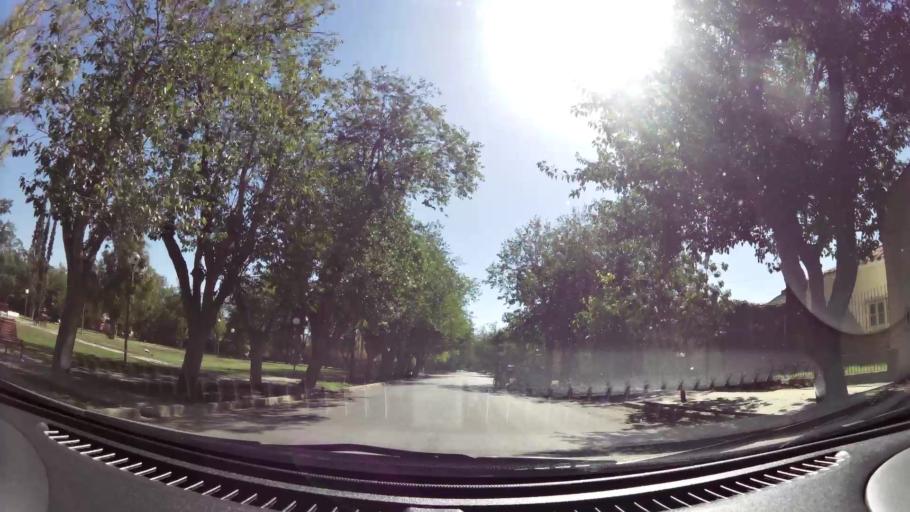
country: AR
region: Mendoza
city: Mendoza
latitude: -32.8815
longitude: -68.8097
